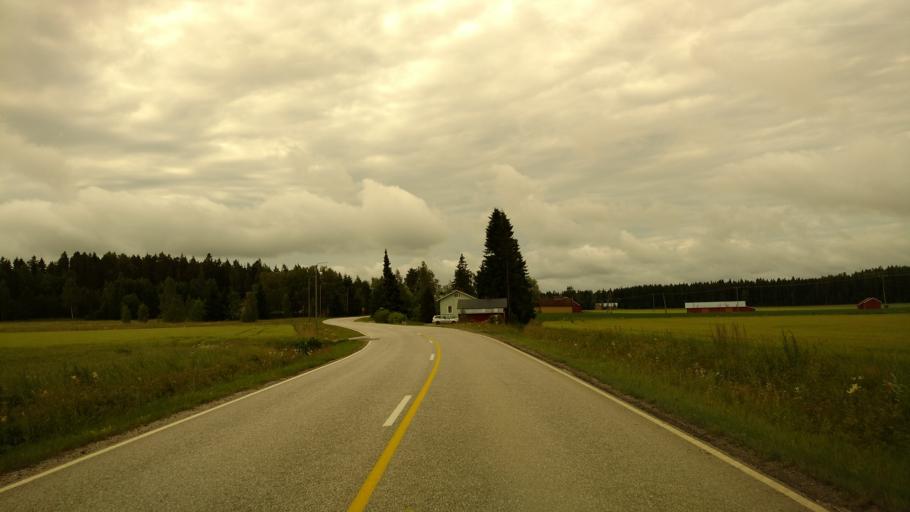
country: FI
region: Varsinais-Suomi
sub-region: Salo
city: Kuusjoki
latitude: 60.4849
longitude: 23.1632
